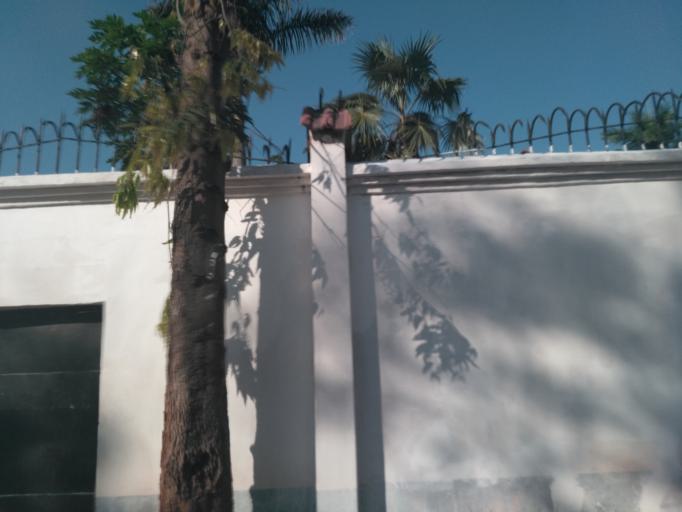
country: TZ
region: Dar es Salaam
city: Magomeni
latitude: -6.7637
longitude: 39.2526
